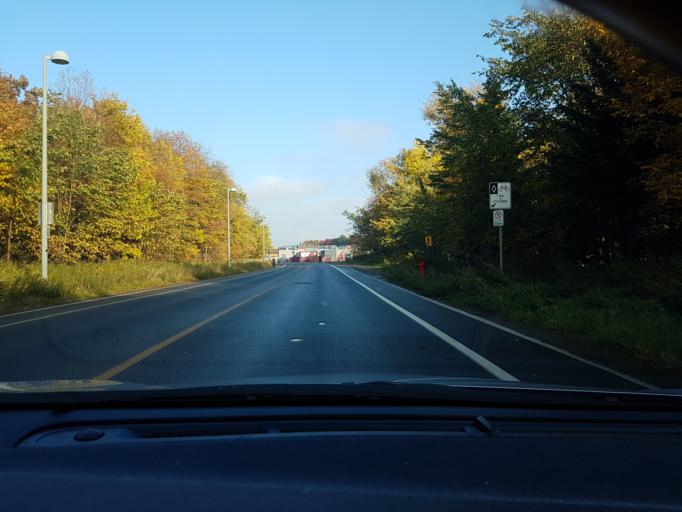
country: CA
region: Quebec
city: L'Ancienne-Lorette
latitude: 46.7964
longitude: -71.3111
